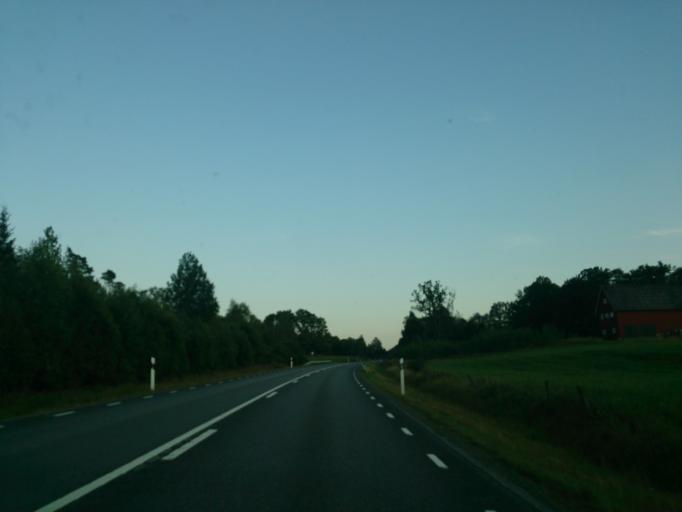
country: SE
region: Joenkoeping
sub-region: Varnamo Kommun
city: Rydaholm
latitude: 57.0280
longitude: 14.2559
